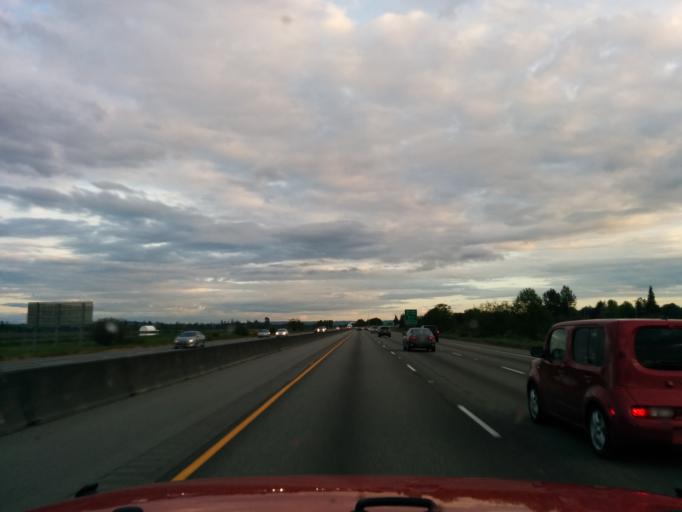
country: US
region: Washington
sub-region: Snohomish County
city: Everett
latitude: 48.0046
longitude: -122.1743
